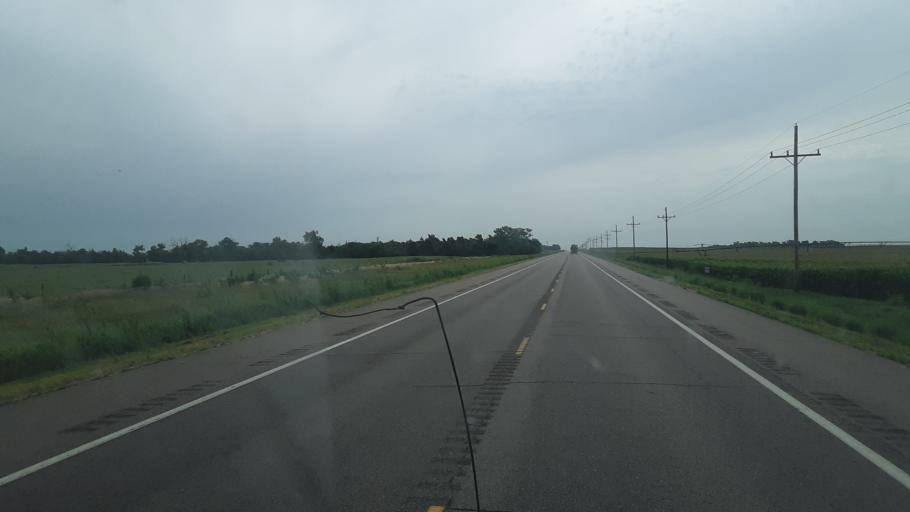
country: US
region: Kansas
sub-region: Edwards County
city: Kinsley
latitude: 37.9275
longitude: -99.3296
